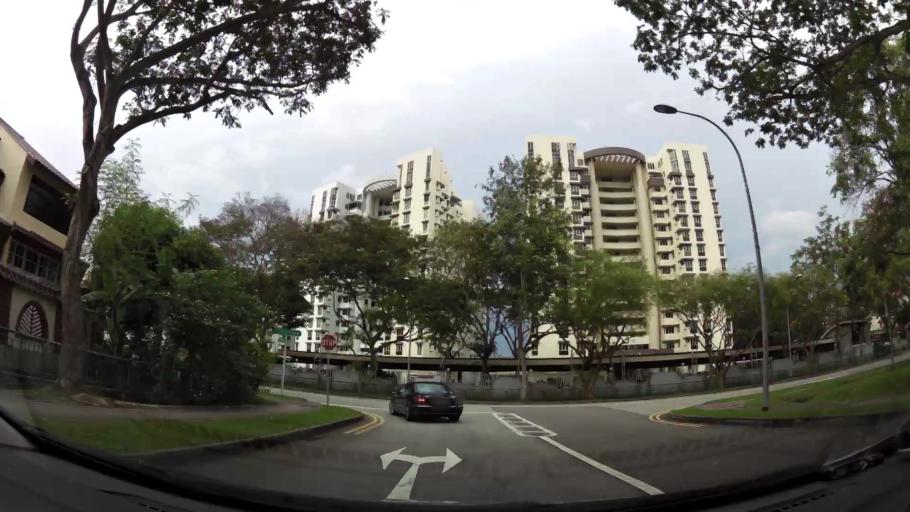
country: MY
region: Johor
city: Kampung Pasir Gudang Baru
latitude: 1.3899
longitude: 103.8369
